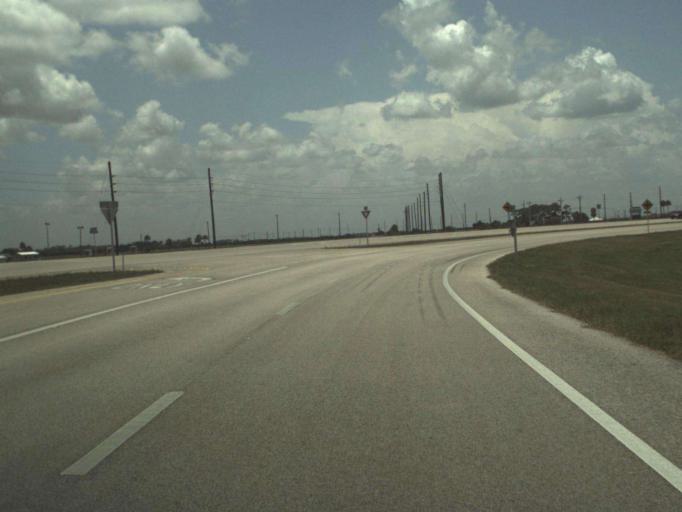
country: US
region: Florida
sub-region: Saint Lucie County
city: Fort Pierce South
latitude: 27.3744
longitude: -80.4838
